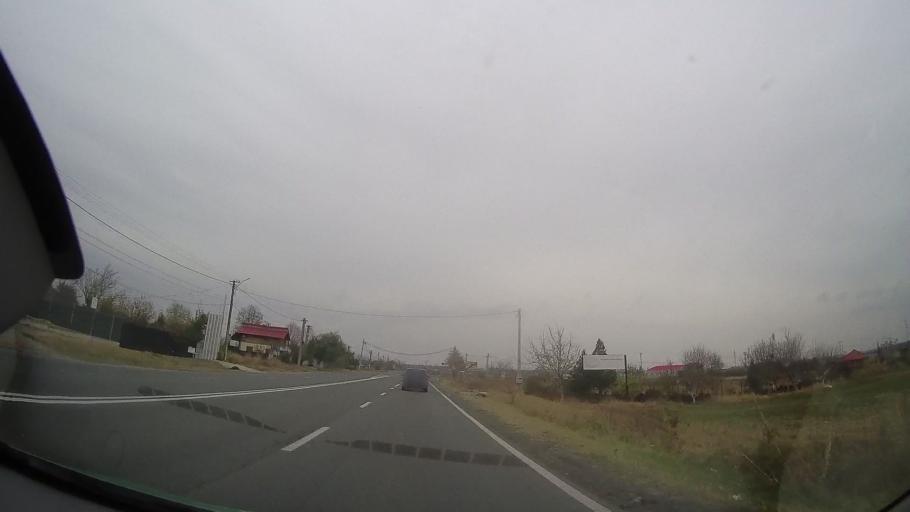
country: RO
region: Prahova
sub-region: Comuna Albesti-Paleologu
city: Albesti-Paleologu
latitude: 44.9549
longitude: 26.2097
